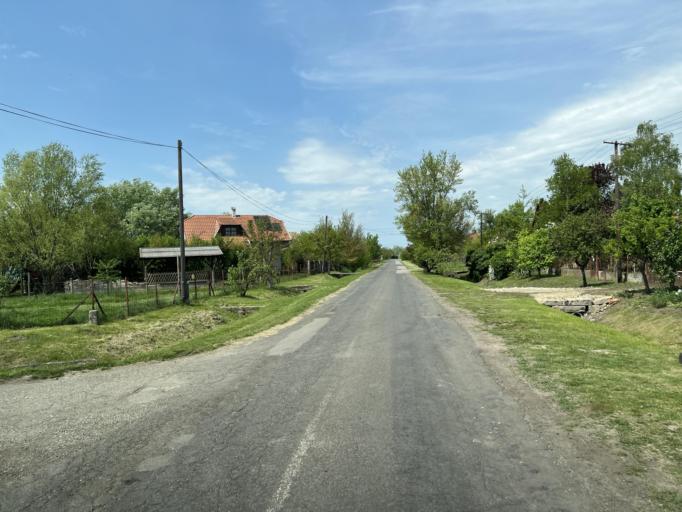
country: HU
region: Pest
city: Tapiogyorgye
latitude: 47.3270
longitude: 19.9583
